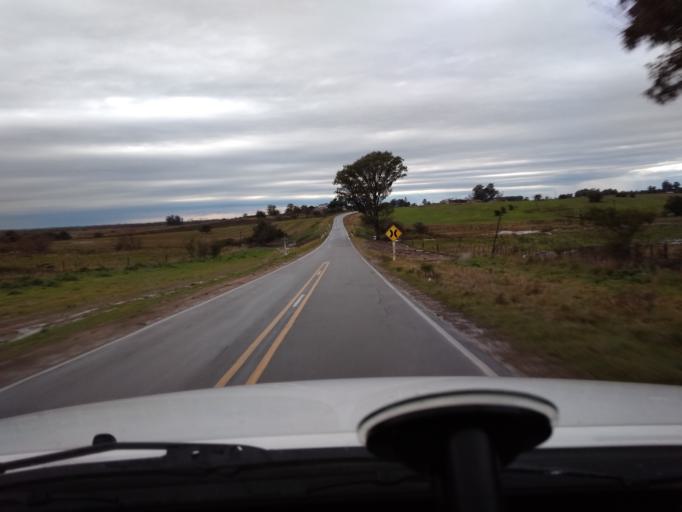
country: UY
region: Canelones
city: San Ramon
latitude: -34.3106
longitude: -55.8909
